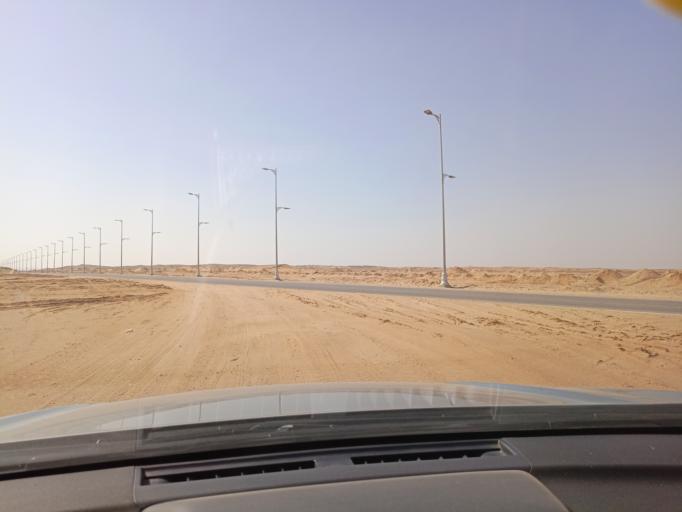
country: EG
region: Muhafazat al Qalyubiyah
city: Al Khankah
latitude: 30.0444
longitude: 31.7126
